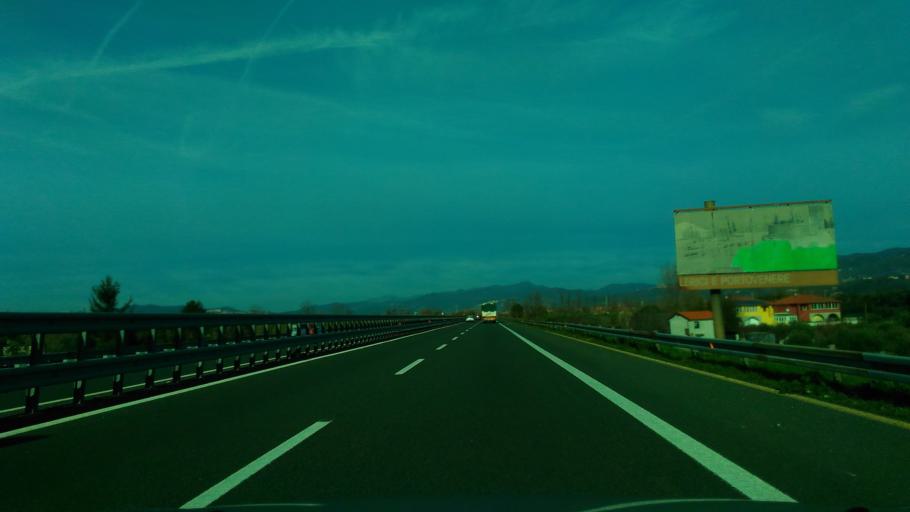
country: IT
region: Liguria
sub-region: Provincia di La Spezia
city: Ameglia
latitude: 44.0855
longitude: 9.9742
